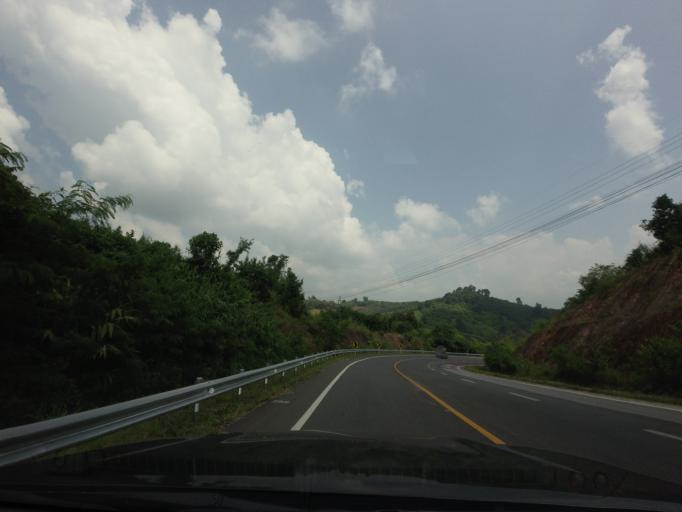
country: TH
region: Nan
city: Santi Suk
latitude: 18.9270
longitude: 100.8964
